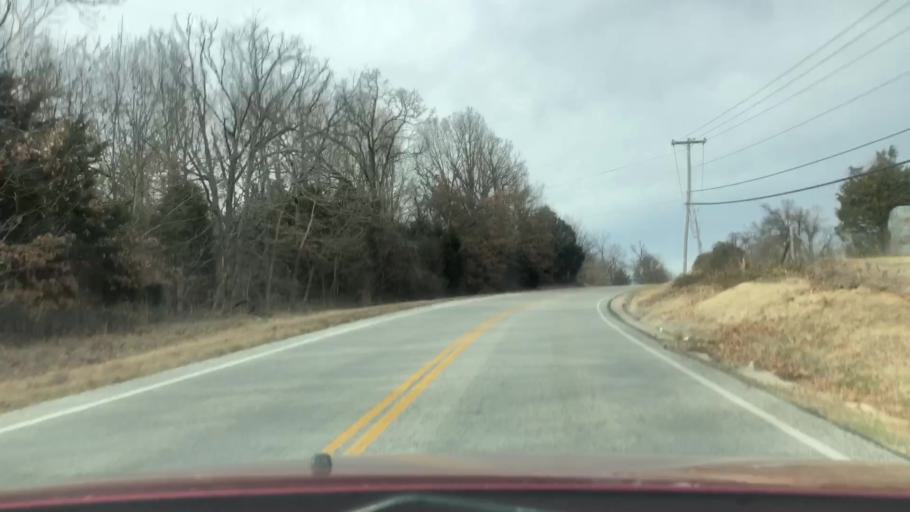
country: US
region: Missouri
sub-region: Greene County
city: Springfield
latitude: 37.2825
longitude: -93.2640
